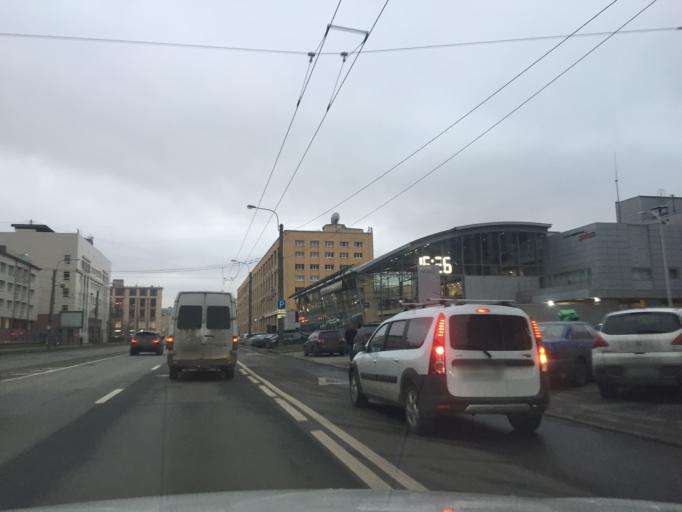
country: RU
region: St.-Petersburg
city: Petrogradka
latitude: 59.9734
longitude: 30.3158
